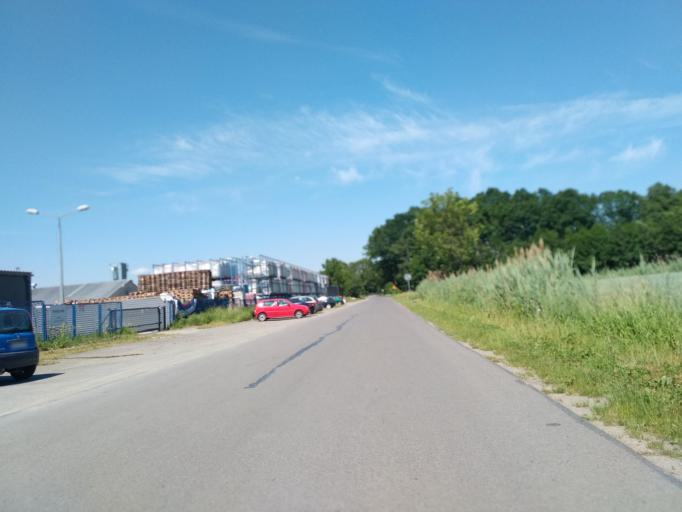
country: PL
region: Subcarpathian Voivodeship
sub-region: Powiat krosnienski
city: Korczyna
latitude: 49.7162
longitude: 21.7858
